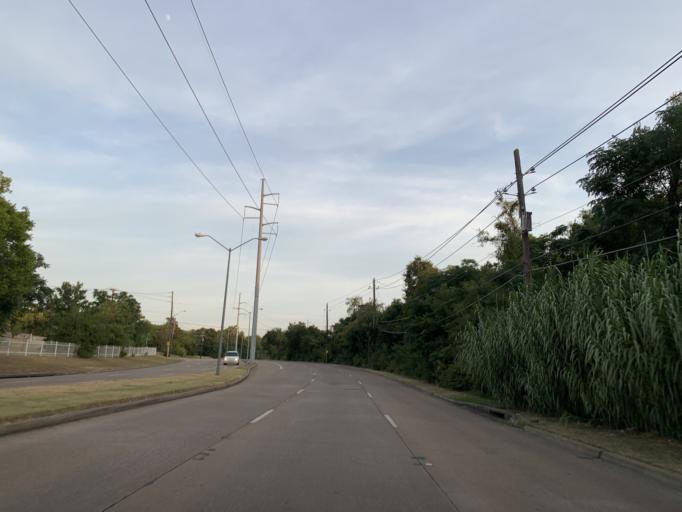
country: US
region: Texas
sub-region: Dallas County
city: Cockrell Hill
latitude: 32.7013
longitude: -96.8916
